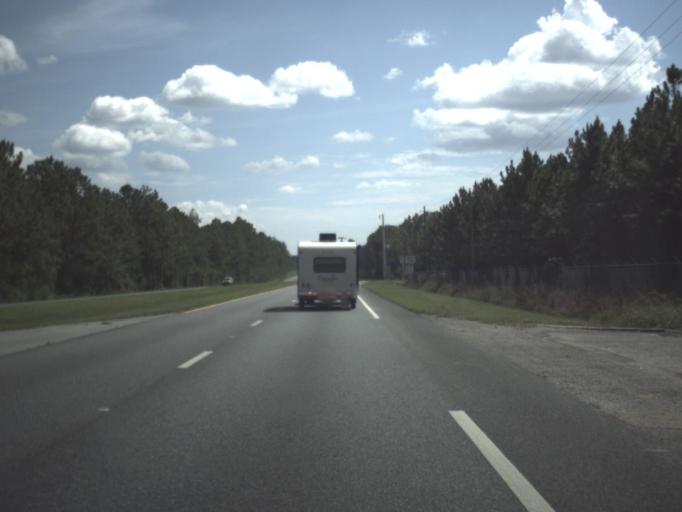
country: US
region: Florida
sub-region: Bay County
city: Youngstown
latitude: 30.3597
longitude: -85.4388
